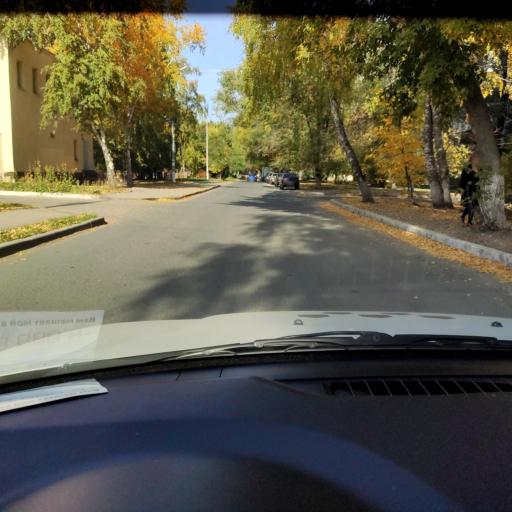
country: RU
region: Samara
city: Tol'yatti
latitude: 53.5039
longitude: 49.4232
